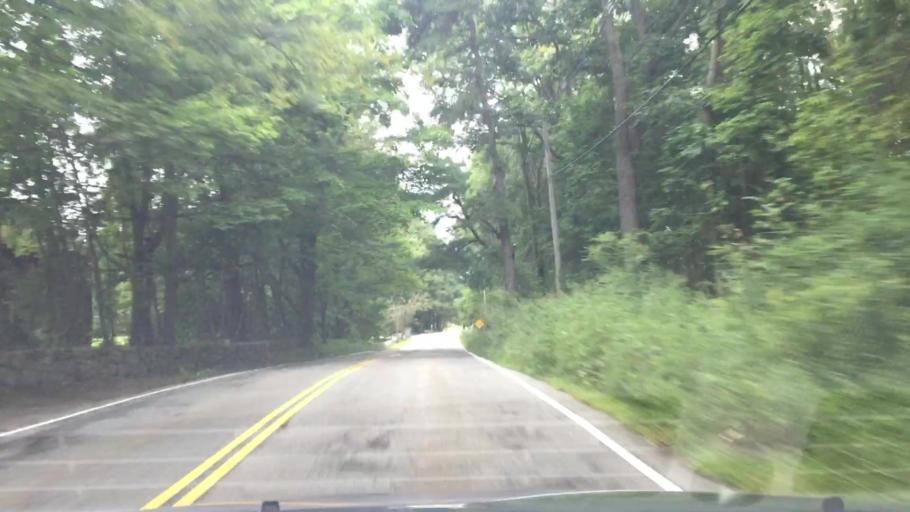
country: US
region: Massachusetts
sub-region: Essex County
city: North Andover
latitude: 42.7042
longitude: -71.0794
